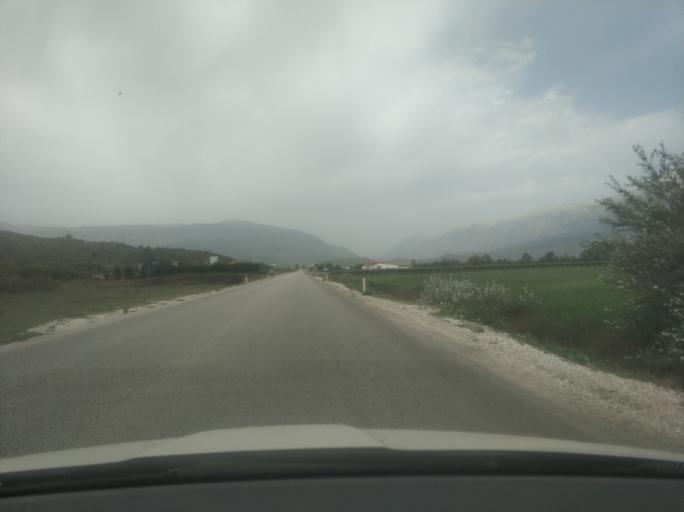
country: AL
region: Gjirokaster
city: Gjirokaster
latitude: 40.1089
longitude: 20.1223
